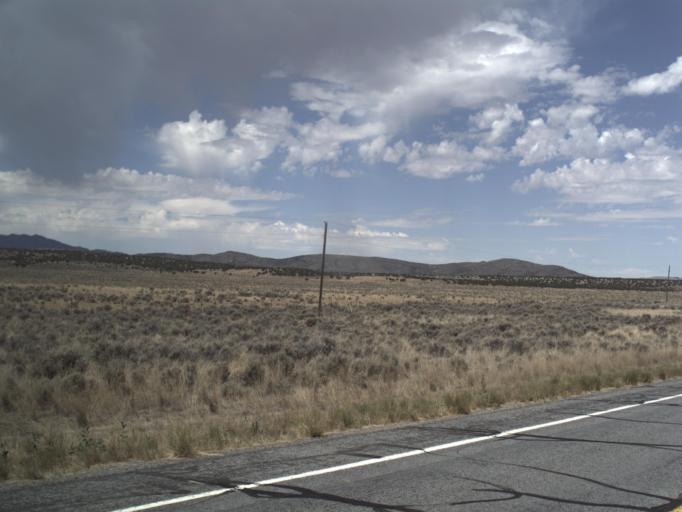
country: US
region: Utah
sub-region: Utah County
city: Eagle Mountain
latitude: 40.0528
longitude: -112.2984
